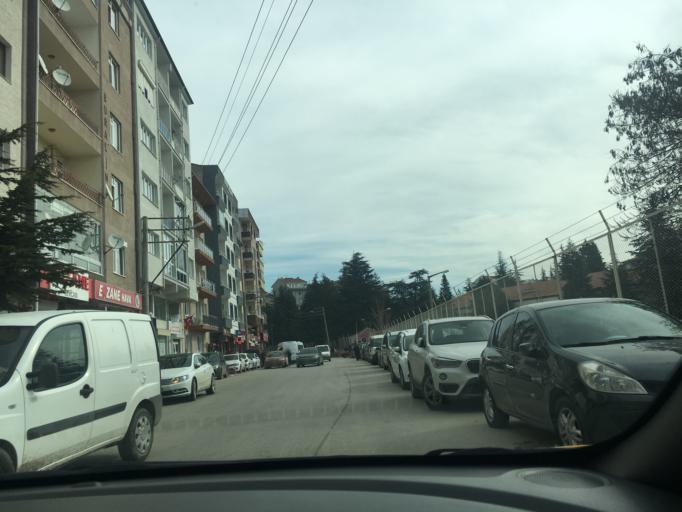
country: TR
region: Eskisehir
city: Eskisehir
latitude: 39.7737
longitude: 30.5100
